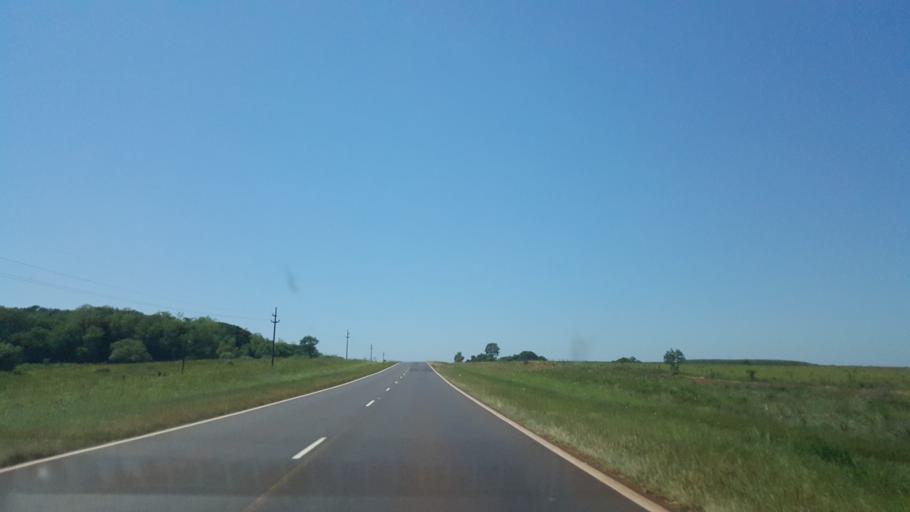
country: AR
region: Corrientes
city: Santo Tome
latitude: -28.3714
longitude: -56.1099
